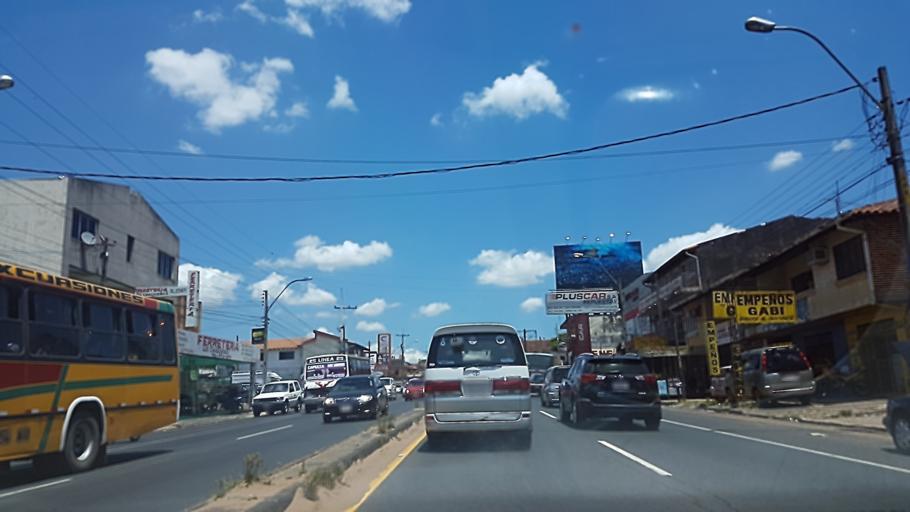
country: PY
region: Central
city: San Lorenzo
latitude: -25.3427
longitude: -57.4926
